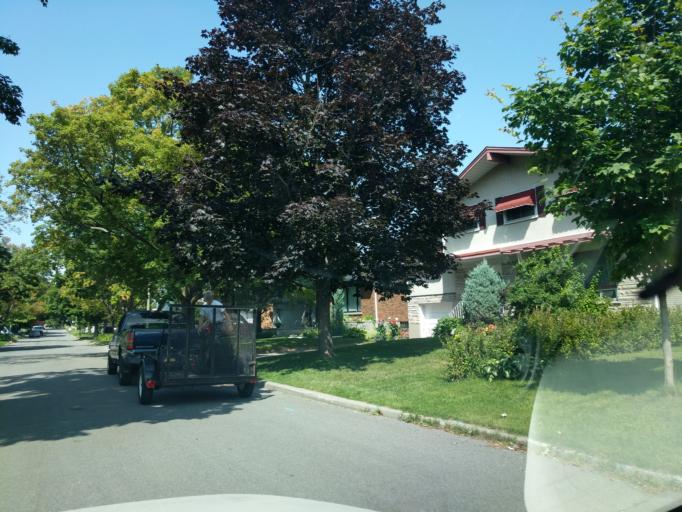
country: CA
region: Ontario
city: Ottawa
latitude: 45.3806
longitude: -75.7541
